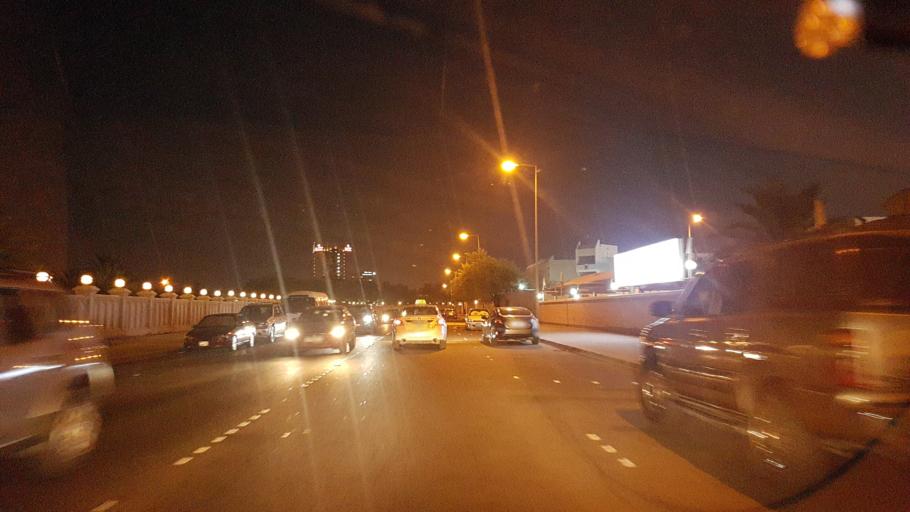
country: BH
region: Manama
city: Manama
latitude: 26.2225
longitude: 50.5949
